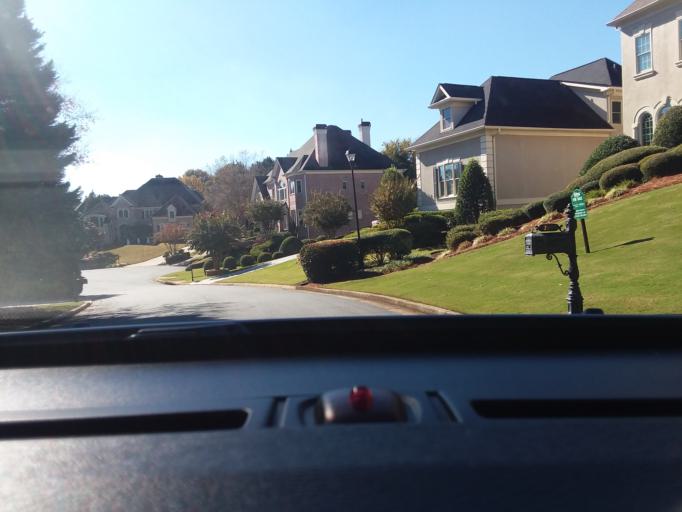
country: US
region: Georgia
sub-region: Fulton County
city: Johns Creek
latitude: 34.0331
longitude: -84.1810
